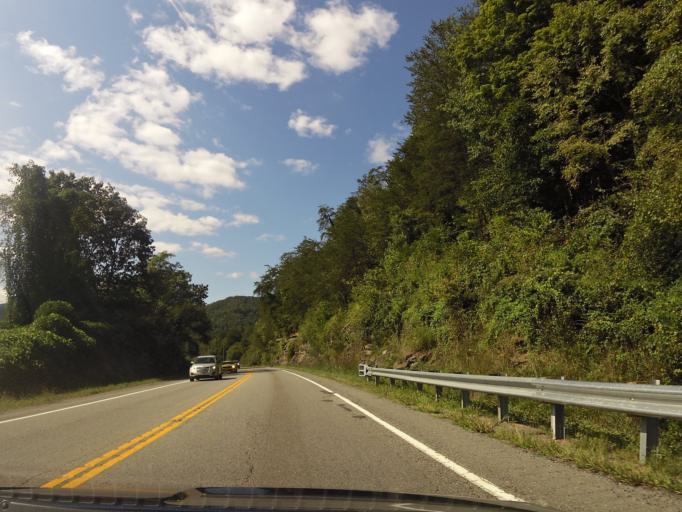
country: US
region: Kentucky
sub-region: Bell County
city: Pineville
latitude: 36.7394
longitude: -83.6741
